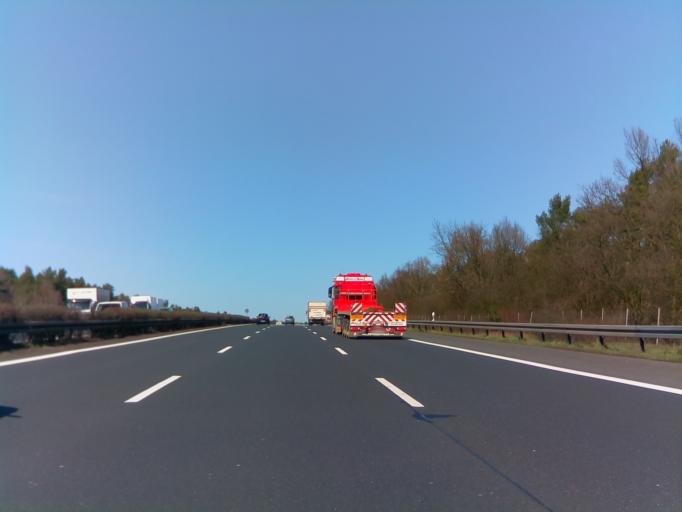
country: DE
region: Brandenburg
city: Fichtenwalde
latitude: 52.2496
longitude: 12.9126
